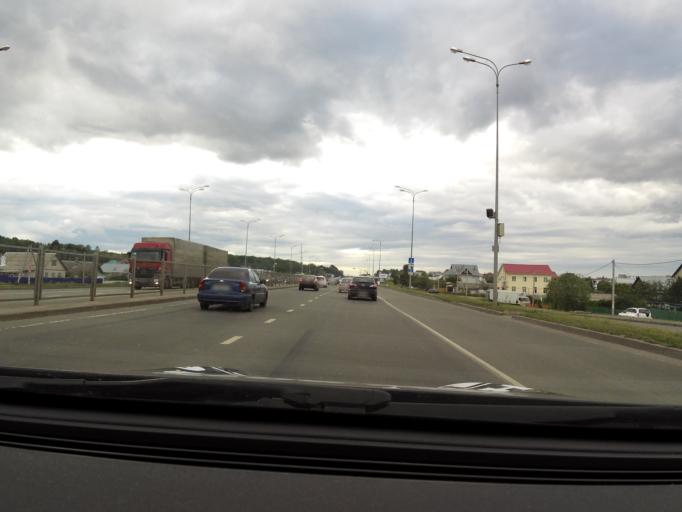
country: RU
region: Tatarstan
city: Osinovo
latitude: 55.8530
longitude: 48.8799
